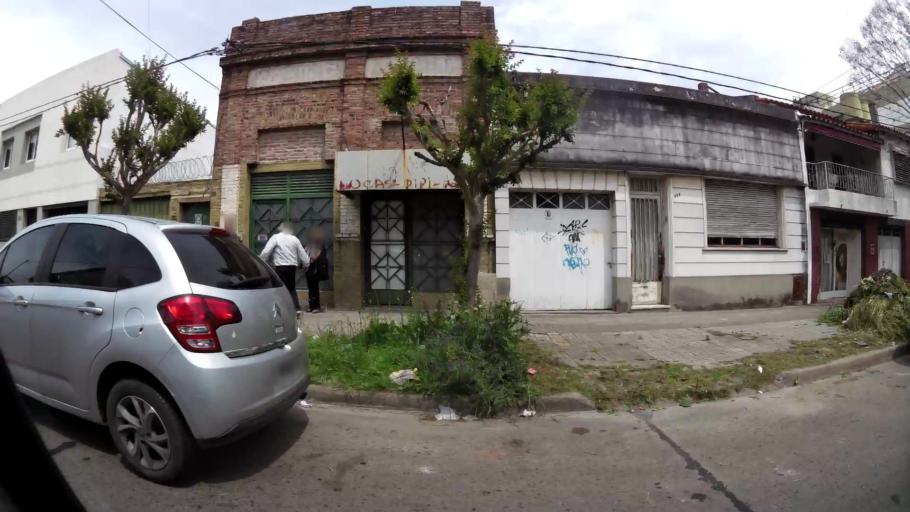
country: AR
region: Buenos Aires
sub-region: Partido de La Plata
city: La Plata
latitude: -34.9317
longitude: -57.9505
